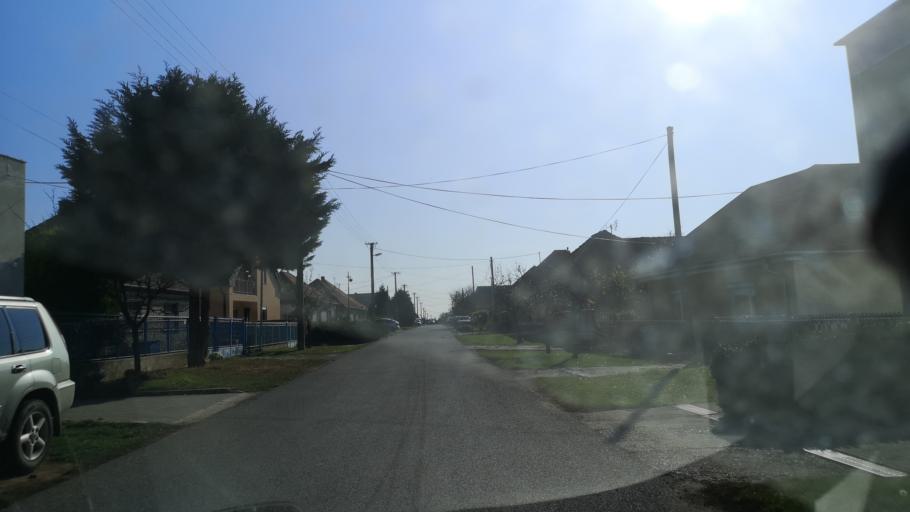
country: SK
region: Nitriansky
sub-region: Okres Nitra
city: Nitra
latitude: 48.3117
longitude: 17.9436
